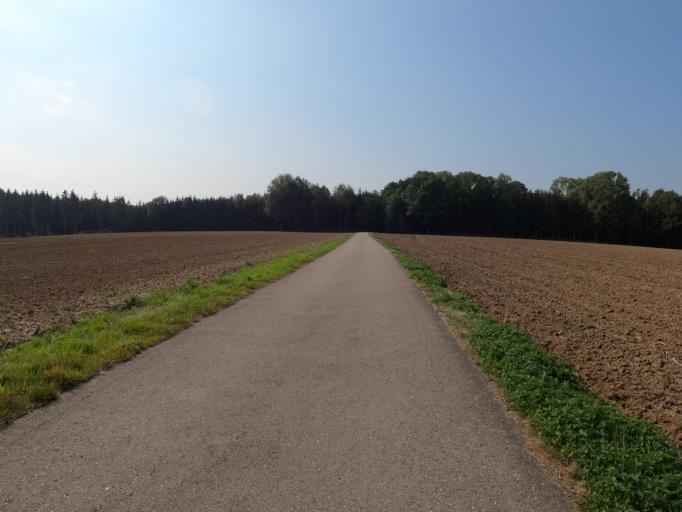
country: DE
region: Bavaria
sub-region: Swabia
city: Rettenbach
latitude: 48.4682
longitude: 10.3296
